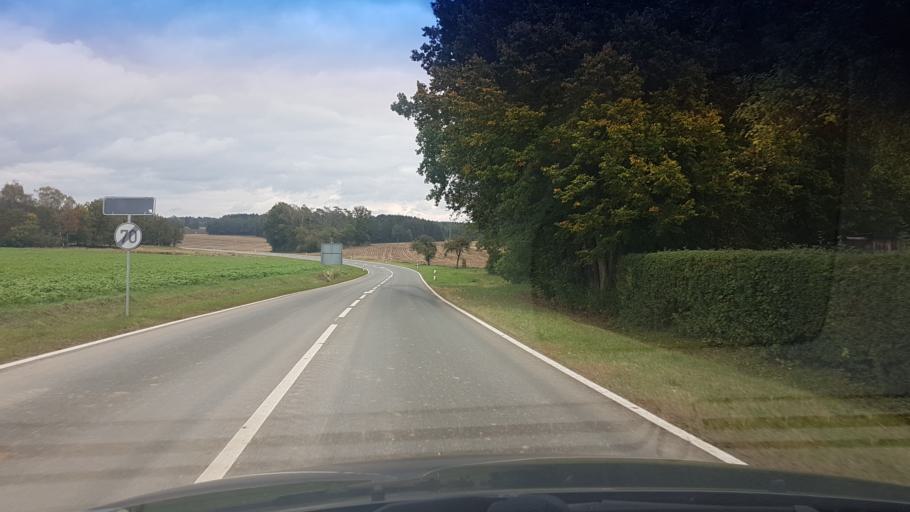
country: DE
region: Bavaria
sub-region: Upper Franconia
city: Stadelhofen
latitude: 50.0161
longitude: 11.2469
